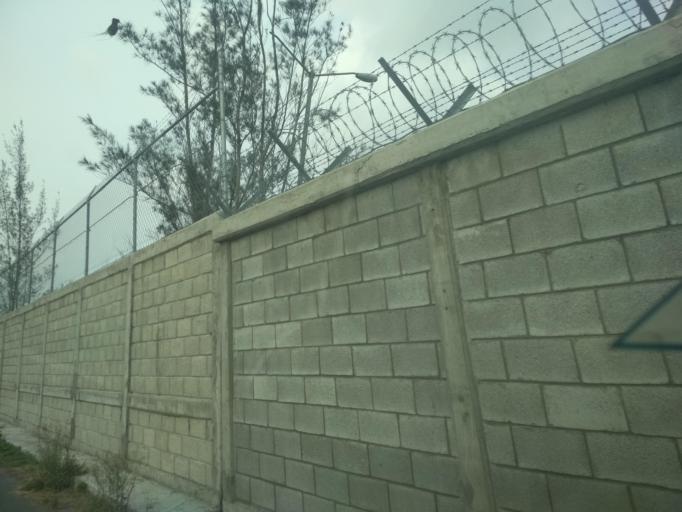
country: MX
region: Veracruz
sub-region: Medellin
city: Fraccionamiento Arboledas San Ramon
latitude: 19.0897
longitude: -96.1477
